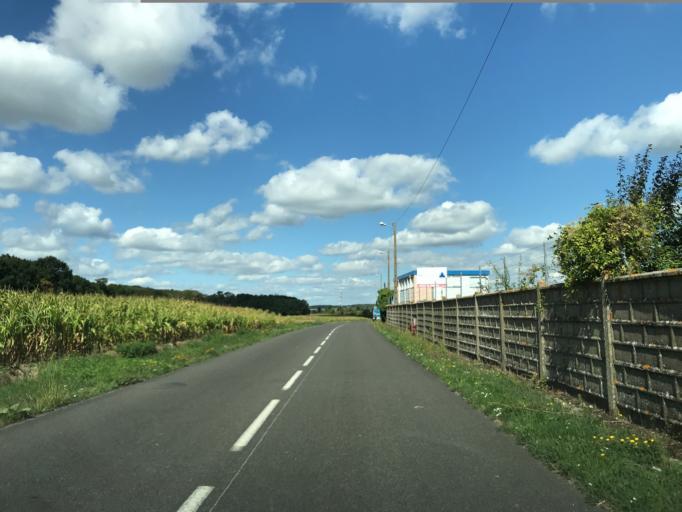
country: FR
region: Haute-Normandie
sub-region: Departement de l'Eure
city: Saint-Just
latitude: 49.1456
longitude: 1.4113
